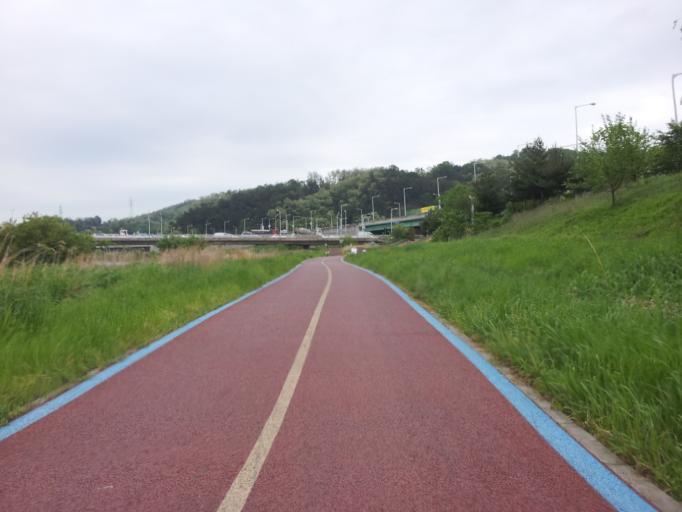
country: KR
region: Daejeon
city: Daejeon
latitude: 36.3768
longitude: 127.4091
